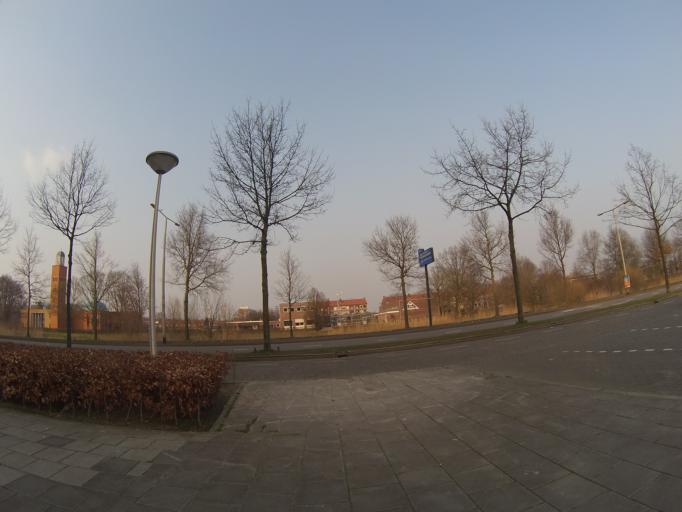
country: NL
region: Utrecht
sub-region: Gemeente Amersfoort
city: Randenbroek
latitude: 52.1640
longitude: 5.4019
